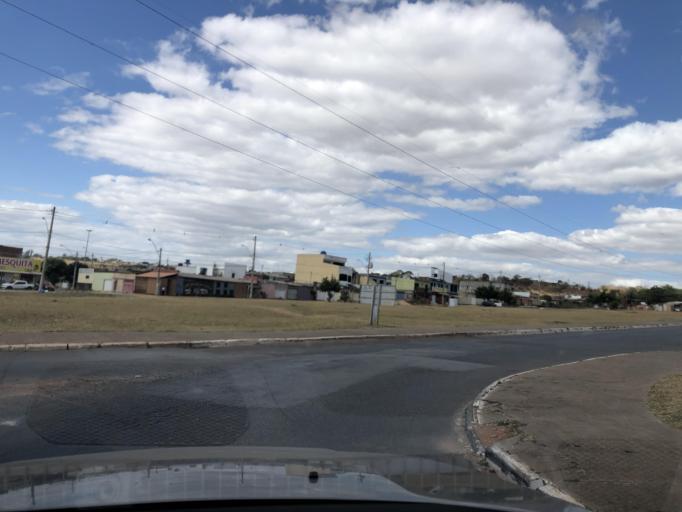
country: BR
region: Federal District
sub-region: Brasilia
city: Brasilia
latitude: -15.8857
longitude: -48.1451
